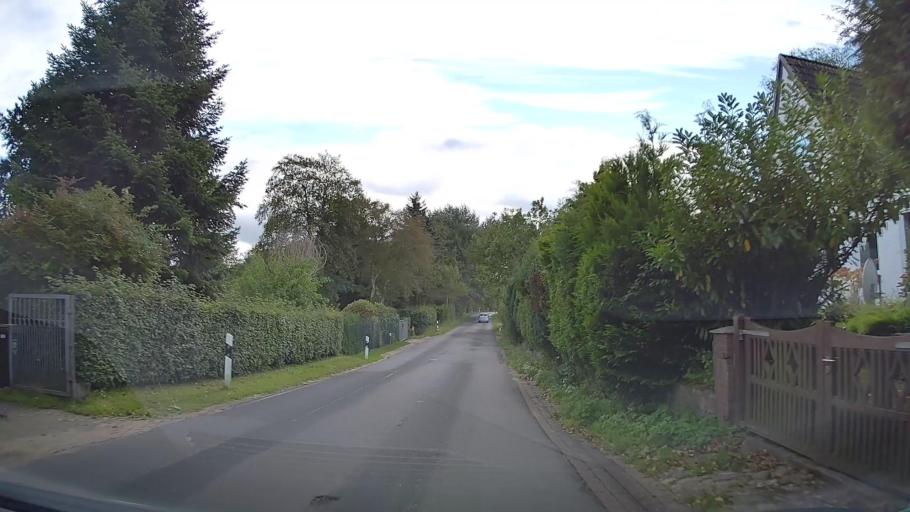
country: DE
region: Schleswig-Holstein
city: Ringsberg
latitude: 54.8336
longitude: 9.5890
